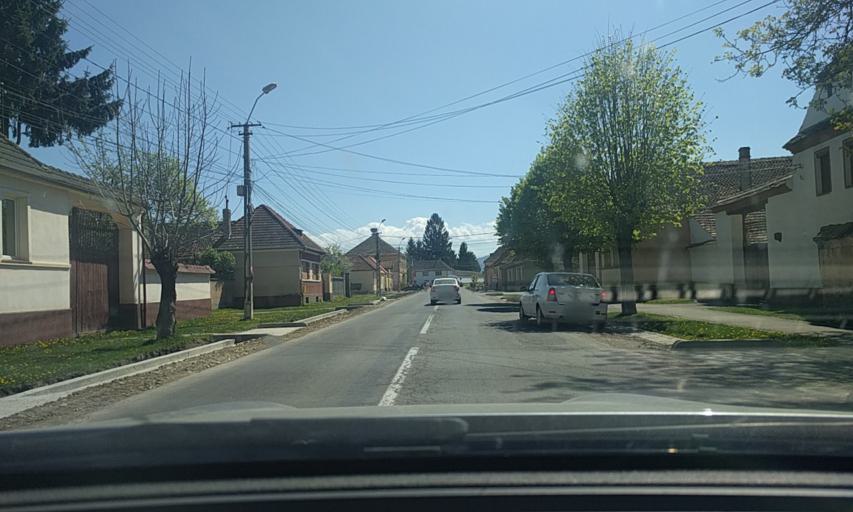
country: RO
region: Brasov
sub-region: Comuna Prejmer
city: Prejmer
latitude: 45.7160
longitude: 25.7781
